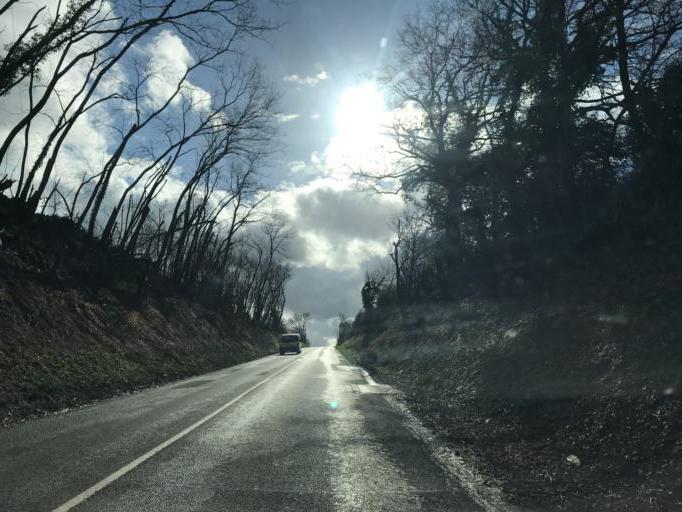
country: FR
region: Rhone-Alpes
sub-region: Departement de l'Ain
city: Sainte-Euphemie
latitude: 45.9613
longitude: 4.8001
